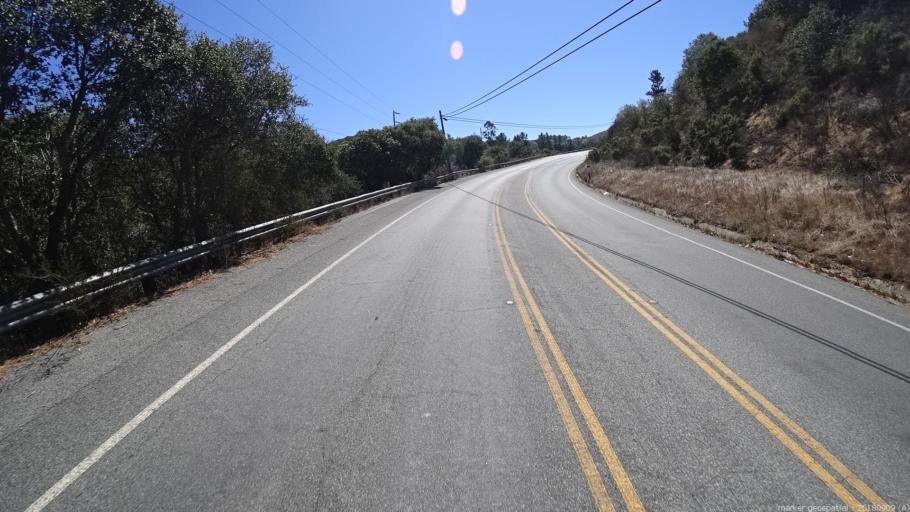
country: US
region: California
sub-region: Monterey County
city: Carmel Valley Village
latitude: 36.5622
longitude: -121.7495
